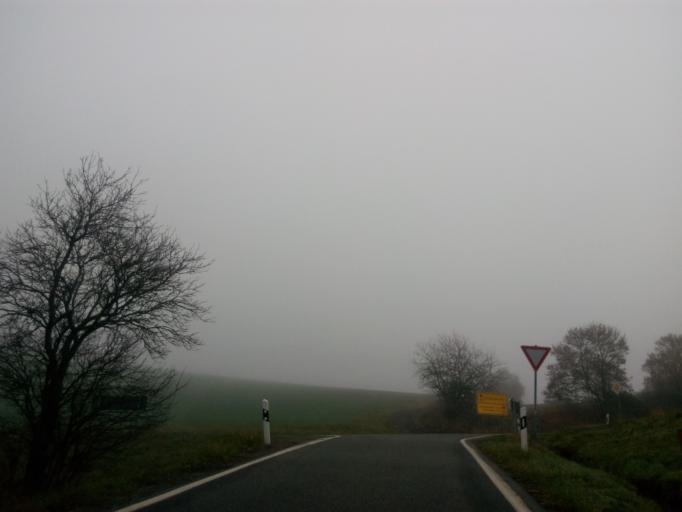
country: DE
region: Rheinland-Pfalz
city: Sienhachenbach
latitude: 49.6960
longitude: 7.4862
